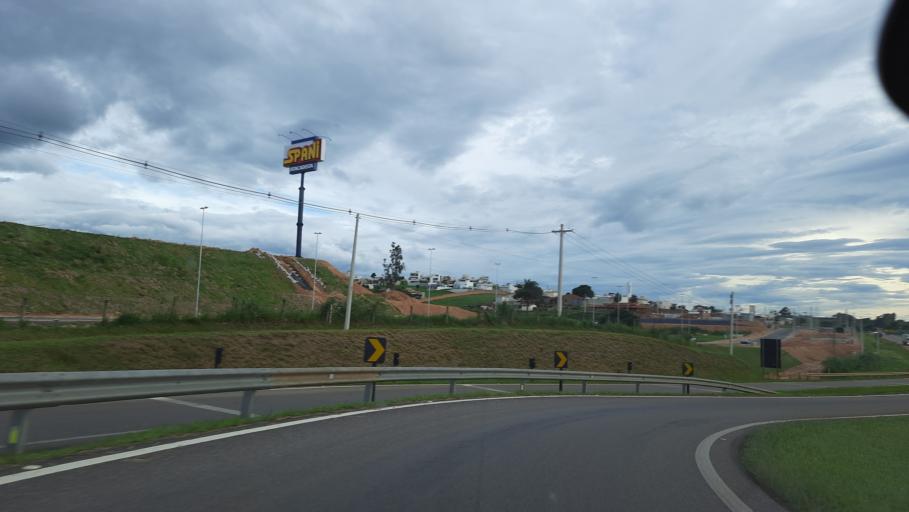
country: BR
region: Sao Paulo
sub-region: Sao Joao Da Boa Vista
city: Sao Joao da Boa Vista
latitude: -21.9906
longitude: -46.7912
